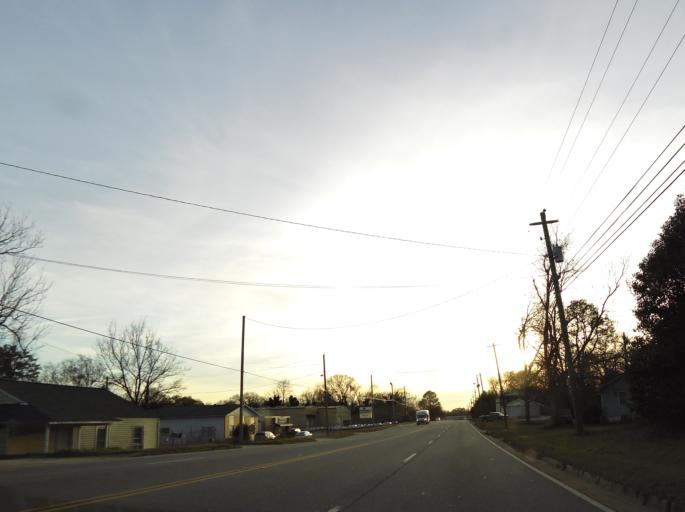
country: US
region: Georgia
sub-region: Bibb County
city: Macon
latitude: 32.7945
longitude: -83.6441
